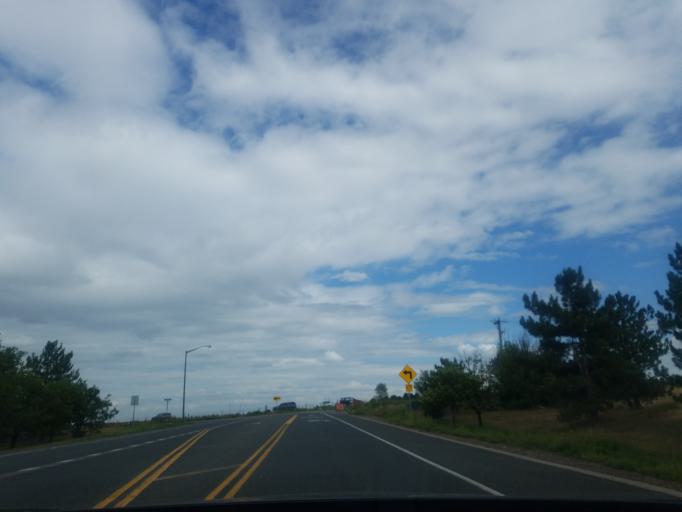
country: US
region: Colorado
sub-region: Weld County
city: Windsor
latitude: 40.4502
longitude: -104.9934
